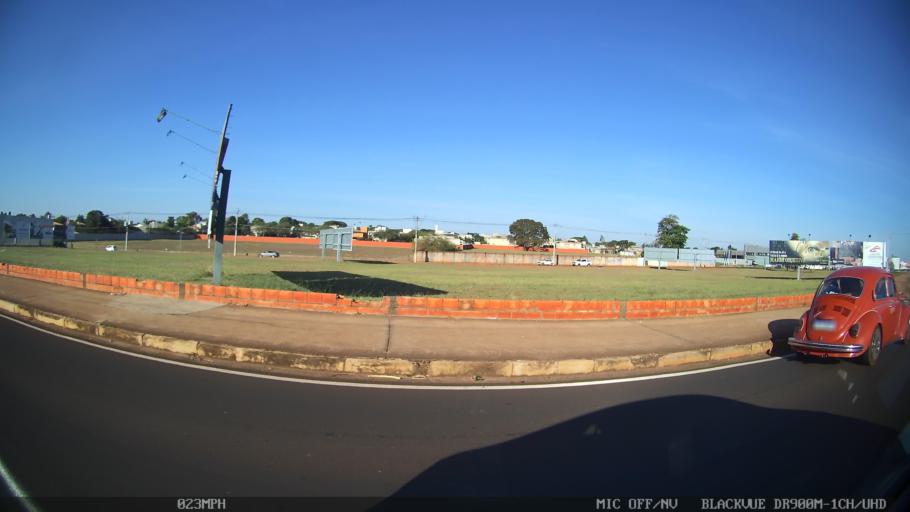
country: BR
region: Sao Paulo
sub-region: Sao Jose Do Rio Preto
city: Sao Jose do Rio Preto
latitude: -20.8521
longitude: -49.4134
